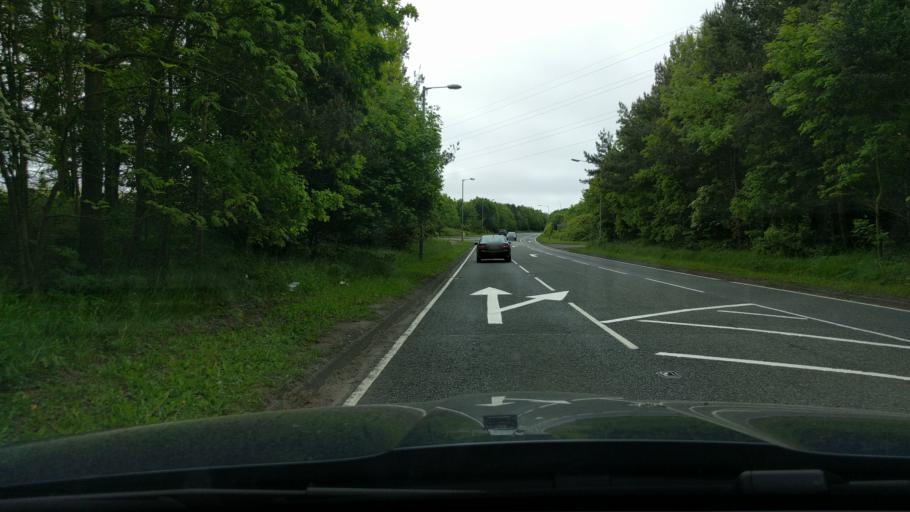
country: GB
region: England
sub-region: Northumberland
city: Cresswell
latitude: 55.2172
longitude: -1.5711
